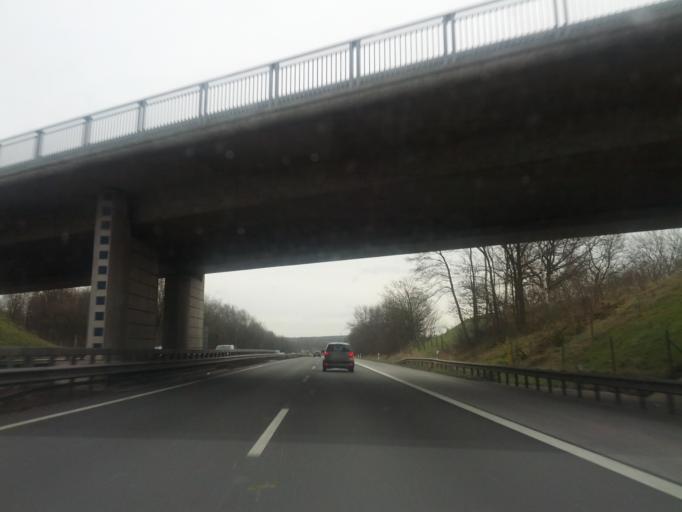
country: DE
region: Lower Saxony
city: Seevetal
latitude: 53.3808
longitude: 9.9875
